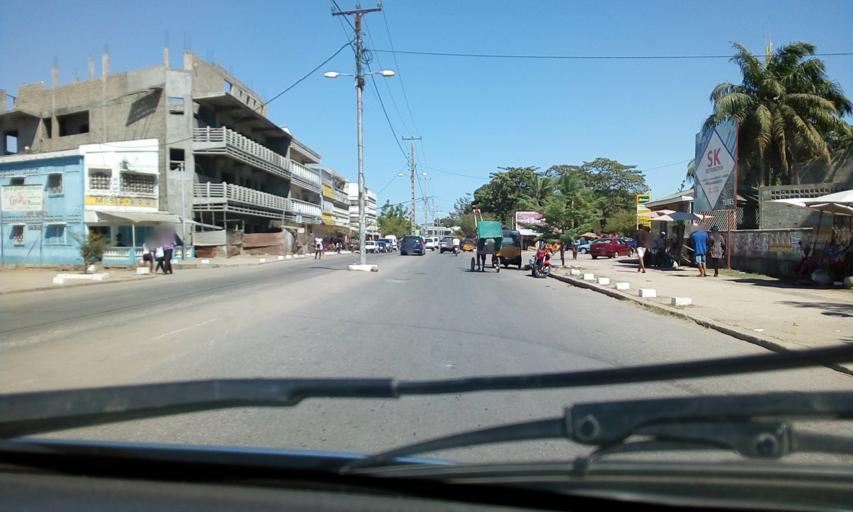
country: MG
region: Boeny
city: Mahajanga
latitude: -15.7202
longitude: 46.3145
